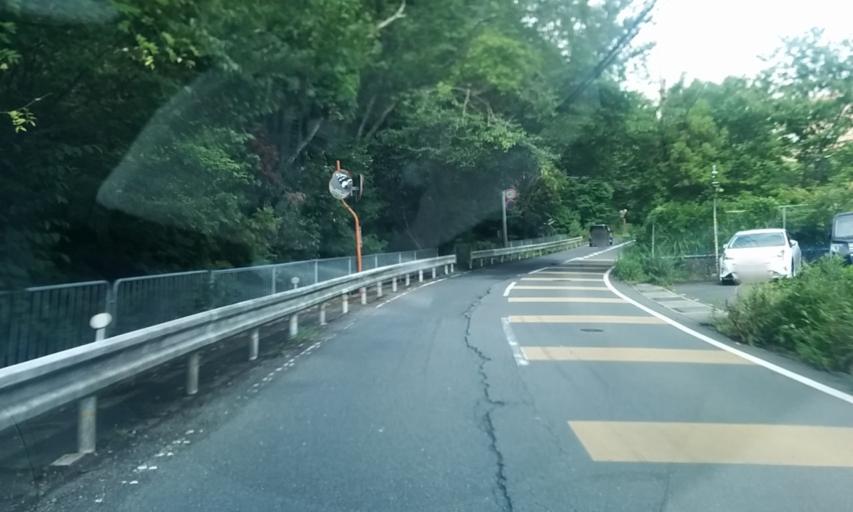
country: JP
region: Kyoto
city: Kameoka
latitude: 35.0169
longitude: 135.5214
